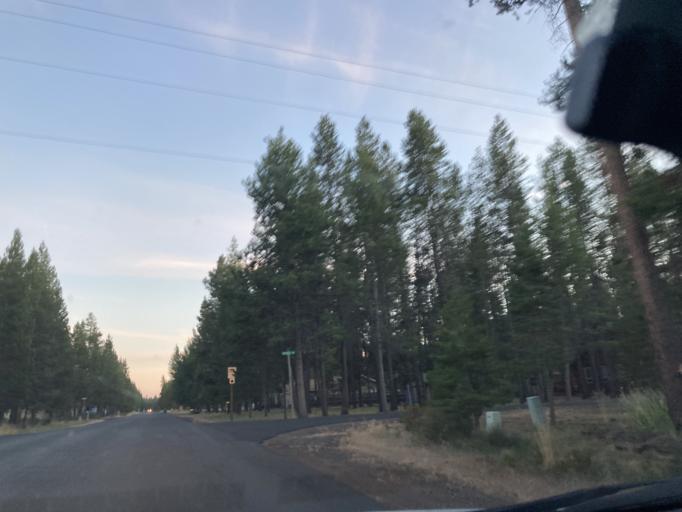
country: US
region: Oregon
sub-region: Deschutes County
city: Three Rivers
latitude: 43.8253
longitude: -121.4656
